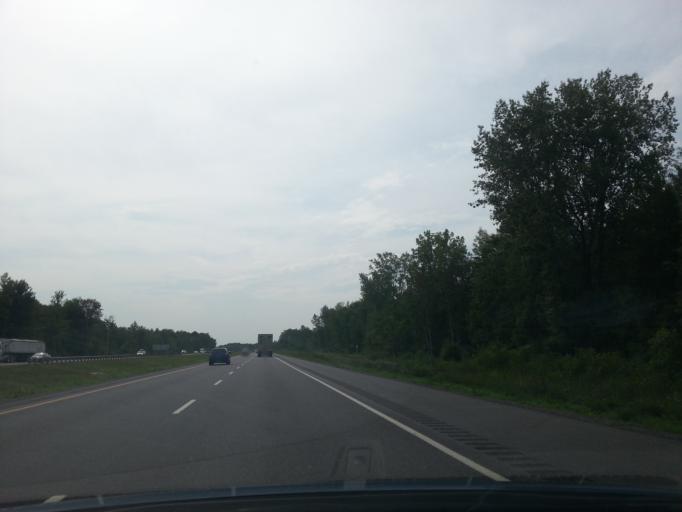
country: CA
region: Quebec
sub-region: Monteregie
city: Mercier
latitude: 45.3371
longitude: -73.7831
